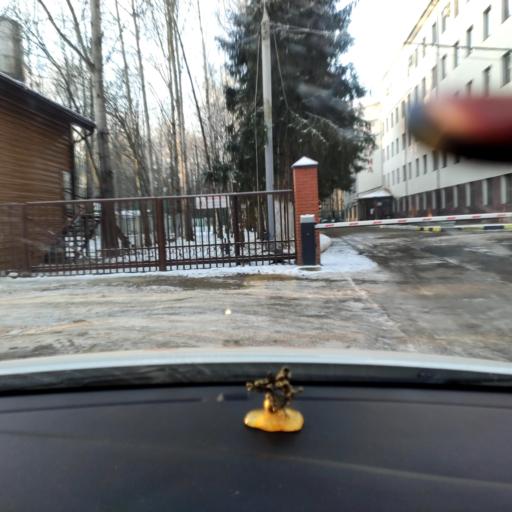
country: RU
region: Tatarstan
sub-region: Gorod Kazan'
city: Kazan
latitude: 55.6766
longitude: 49.0985
